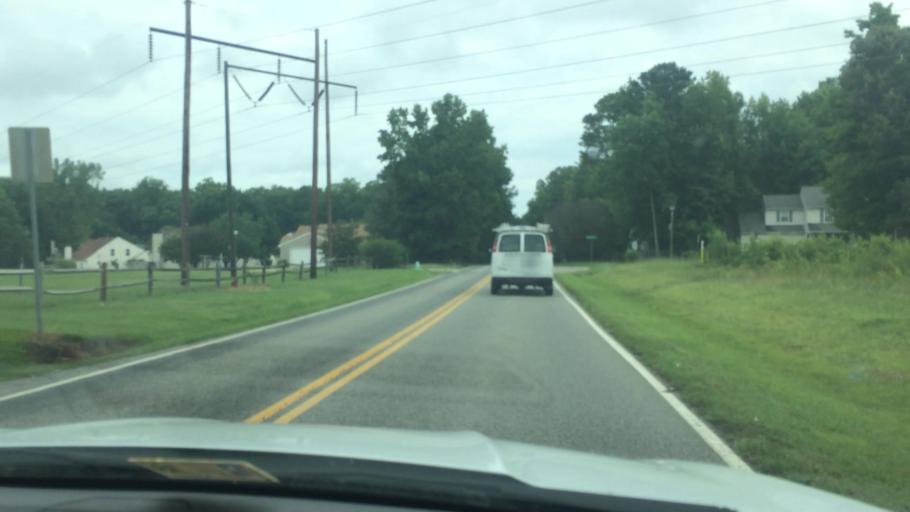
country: US
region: Virginia
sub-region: City of Williamsburg
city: Williamsburg
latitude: 37.2753
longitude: -76.6723
